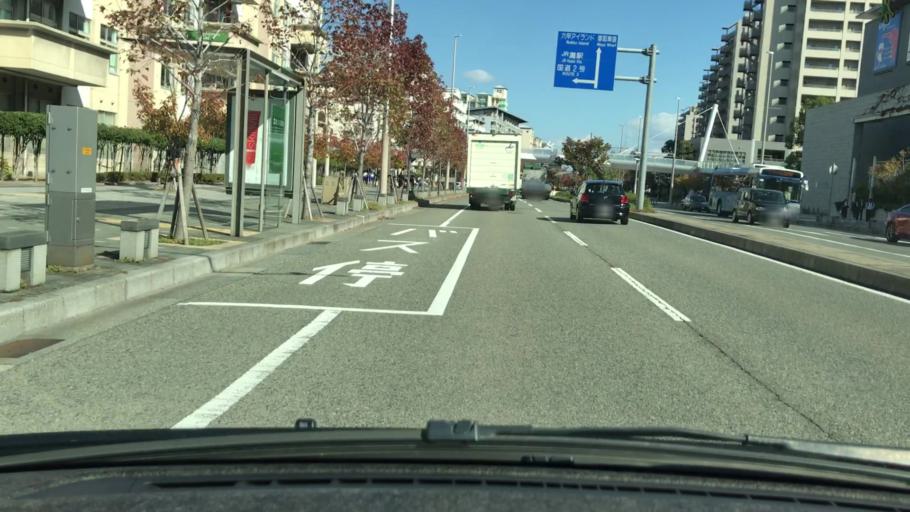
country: JP
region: Hyogo
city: Kobe
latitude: 34.6997
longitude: 135.2172
